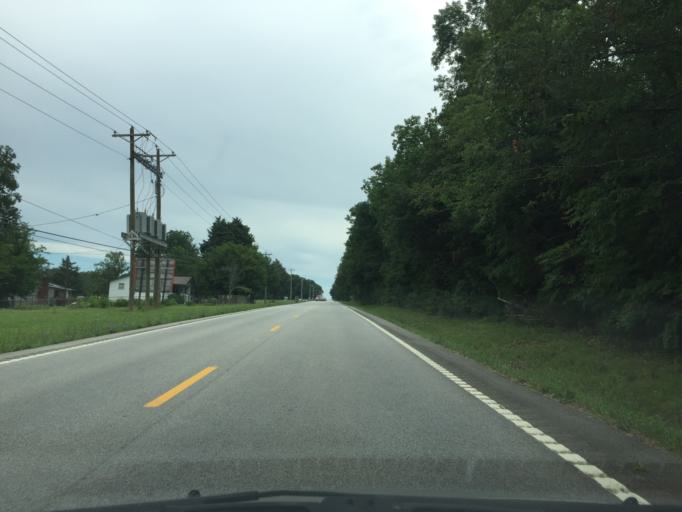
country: US
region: Tennessee
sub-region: Bradley County
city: Hopewell
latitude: 35.2754
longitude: -84.9814
